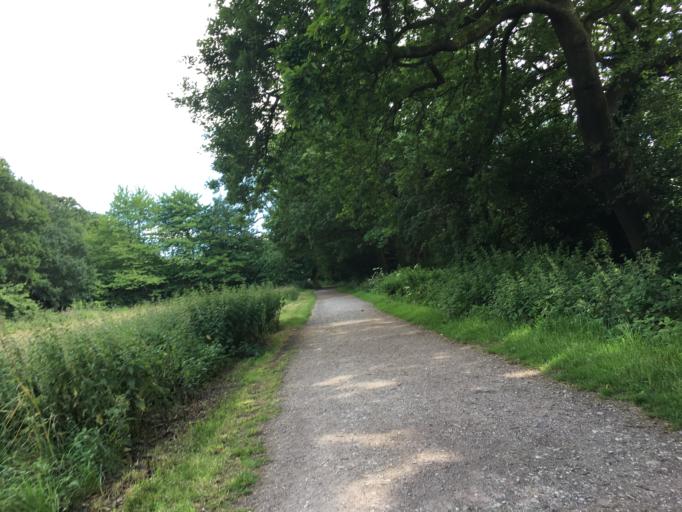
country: GB
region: England
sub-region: Greater London
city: Belsize Park
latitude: 51.5728
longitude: -0.1834
